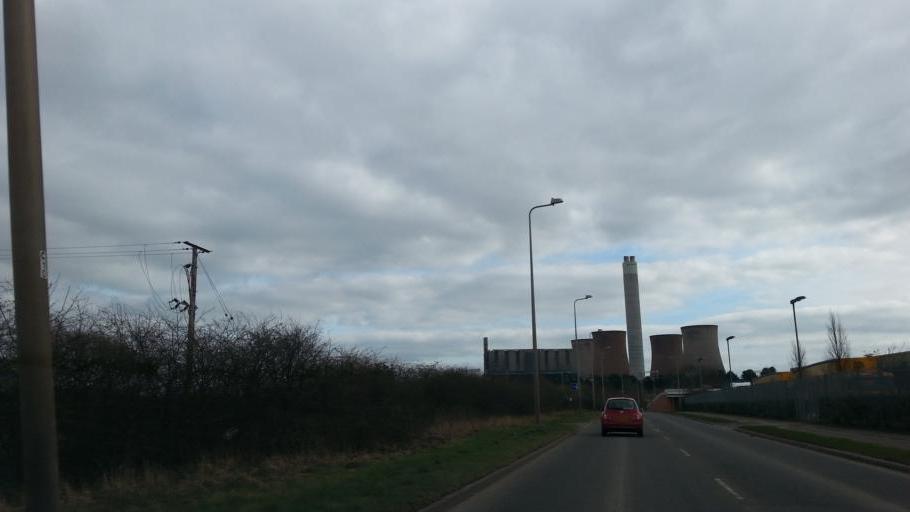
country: GB
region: England
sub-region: Staffordshire
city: Rugeley
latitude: 52.7643
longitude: -1.9281
